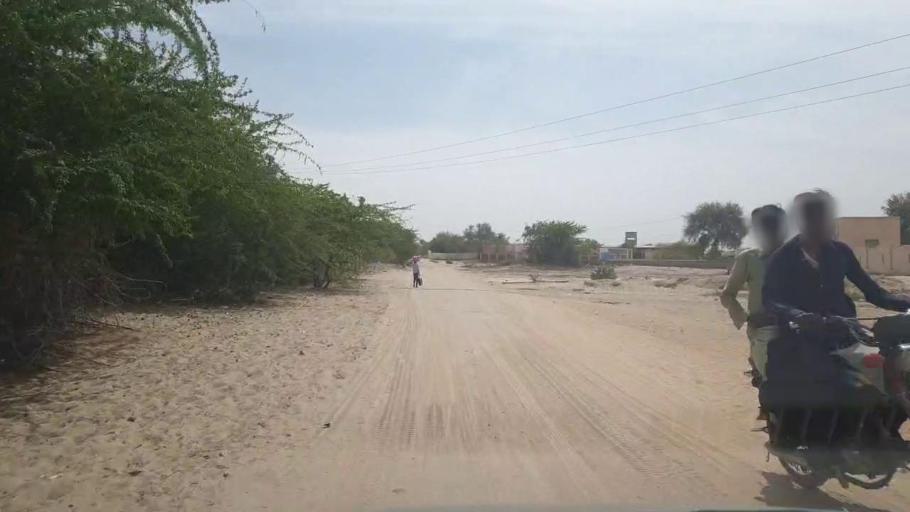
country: PK
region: Sindh
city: Umarkot
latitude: 25.2236
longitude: 69.7136
